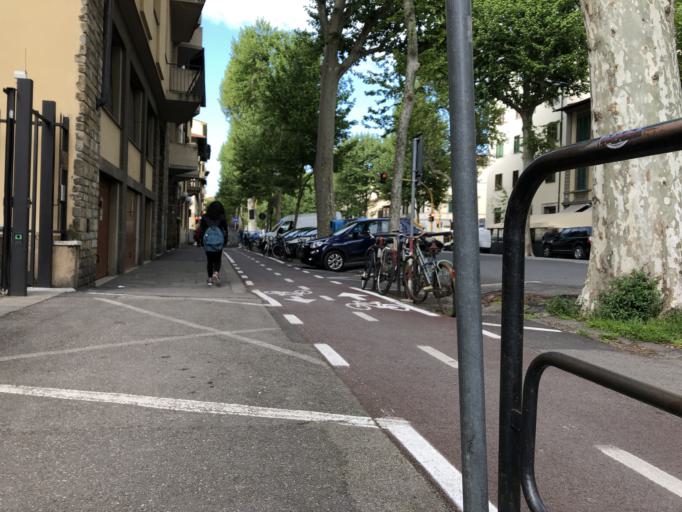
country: IT
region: Tuscany
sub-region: Province of Florence
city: Florence
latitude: 43.7764
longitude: 11.2761
